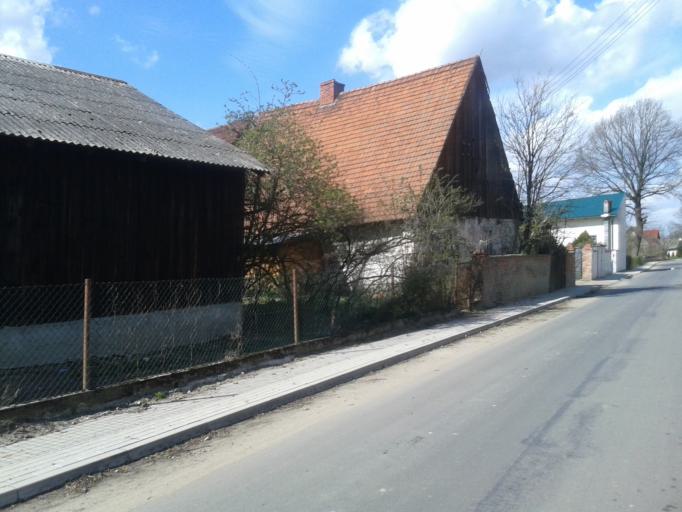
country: PL
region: Lower Silesian Voivodeship
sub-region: Powiat olesnicki
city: Miedzyborz
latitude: 51.4015
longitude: 17.6564
